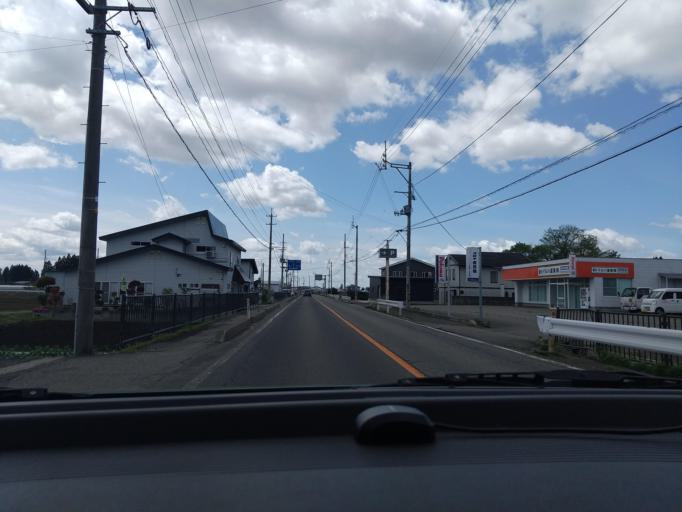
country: JP
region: Akita
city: Kakunodatemachi
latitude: 39.5696
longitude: 140.5611
